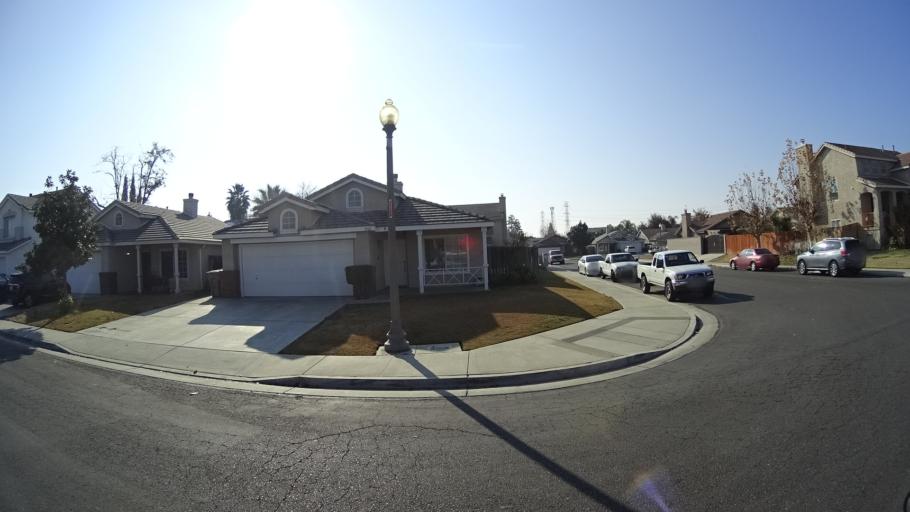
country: US
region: California
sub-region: Kern County
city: Greenacres
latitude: 35.3216
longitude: -119.0933
